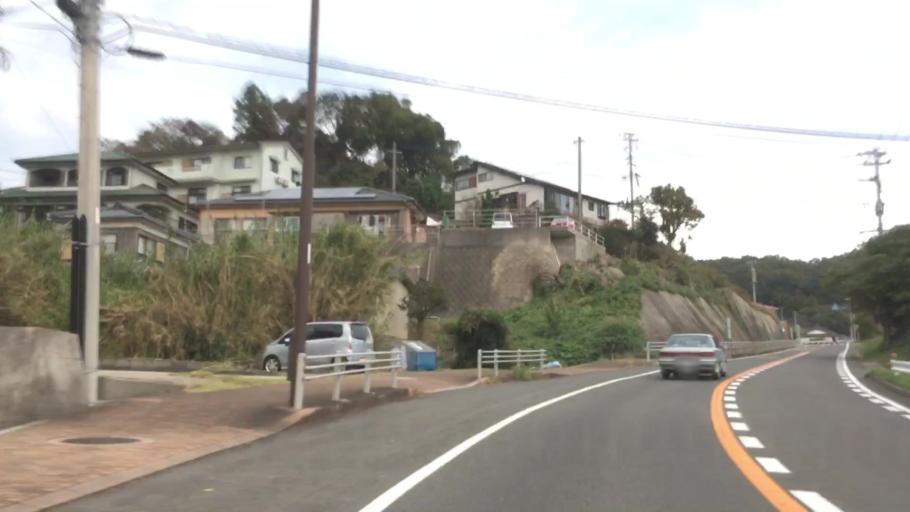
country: JP
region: Nagasaki
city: Togitsu
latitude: 32.9345
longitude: 129.6484
